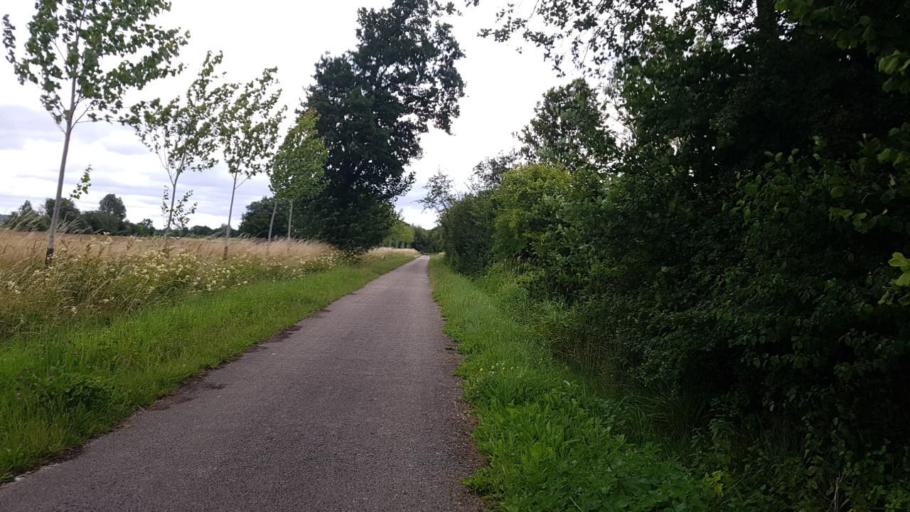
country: FR
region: Picardie
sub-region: Departement de l'Aisne
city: Buironfosse
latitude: 49.9029
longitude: 3.8107
